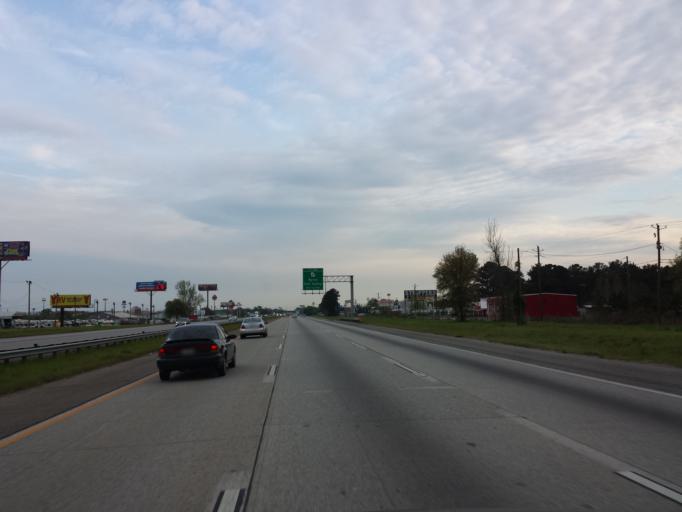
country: US
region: Georgia
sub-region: Peach County
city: Byron
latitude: 32.6701
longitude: -83.7447
